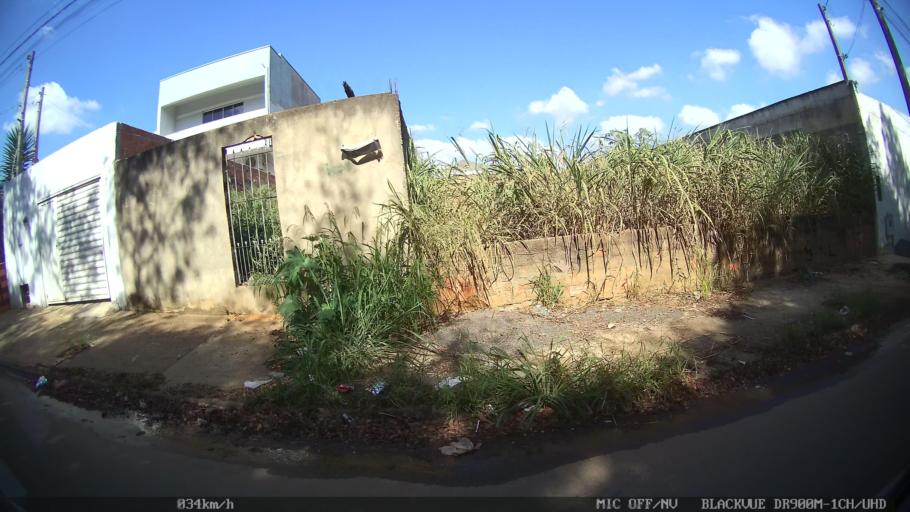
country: BR
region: Sao Paulo
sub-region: Hortolandia
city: Hortolandia
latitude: -22.8737
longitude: -47.2354
